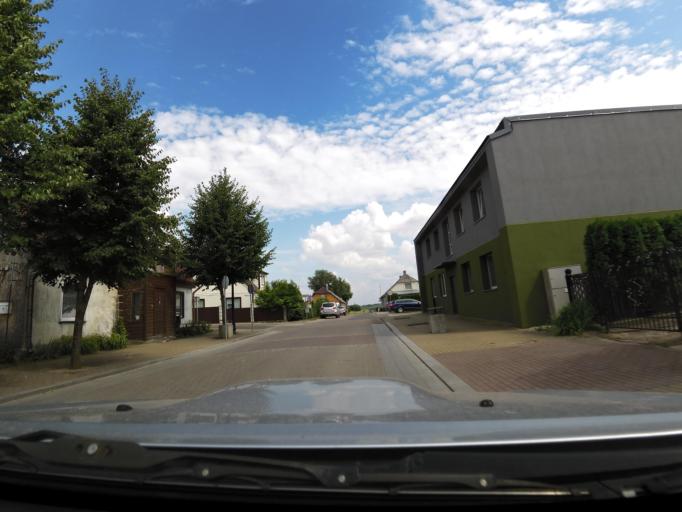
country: LT
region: Taurages apskritis
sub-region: Jurbarkas
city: Jurbarkas
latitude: 55.0768
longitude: 22.7734
